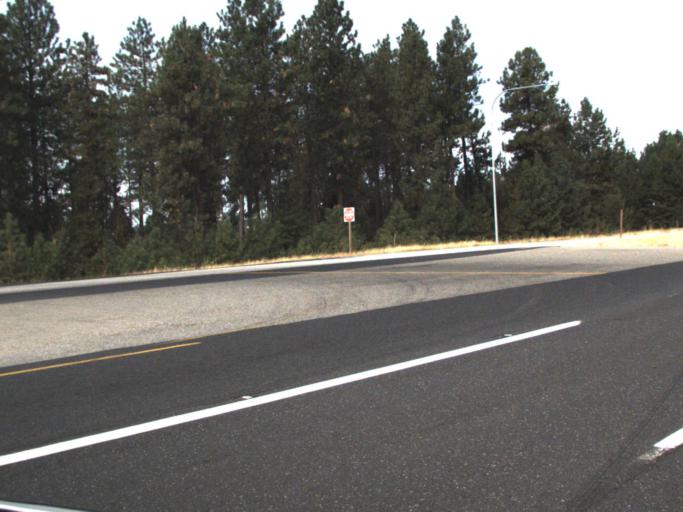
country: US
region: Washington
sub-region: Spokane County
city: Fairwood
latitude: 47.8315
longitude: -117.4190
